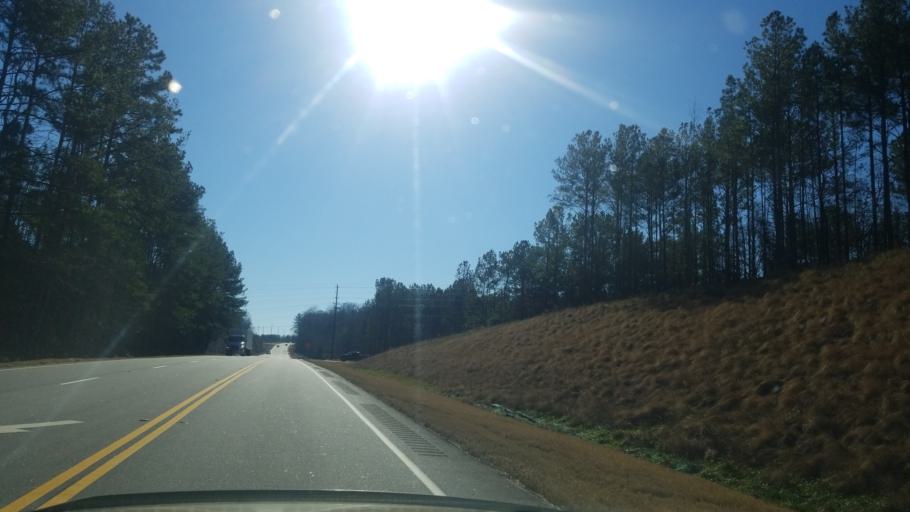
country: US
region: Georgia
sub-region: Troup County
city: West Point
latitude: 32.8623
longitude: -85.1364
